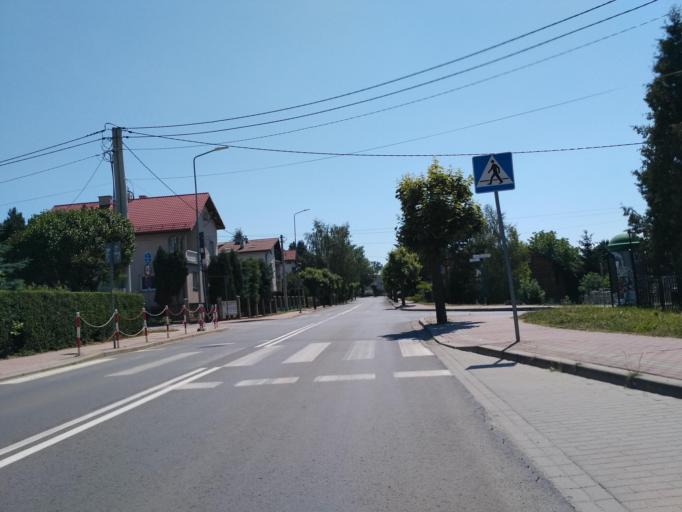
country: PL
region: Subcarpathian Voivodeship
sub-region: Krosno
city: Krosno
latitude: 49.6974
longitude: 21.7710
